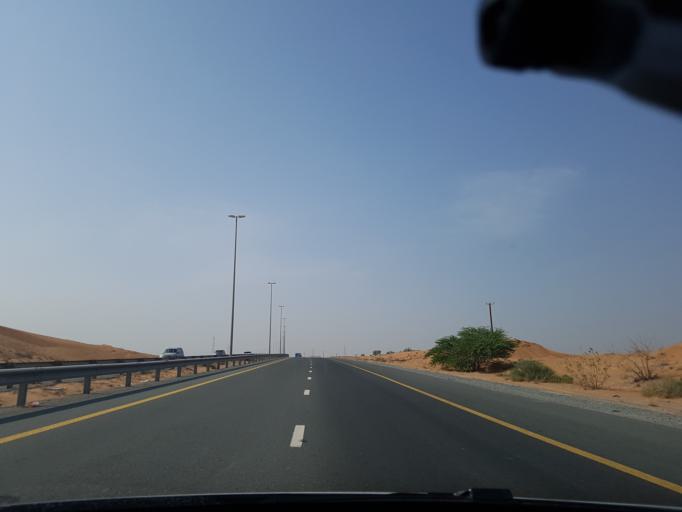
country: AE
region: Umm al Qaywayn
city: Umm al Qaywayn
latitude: 25.5185
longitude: 55.7418
